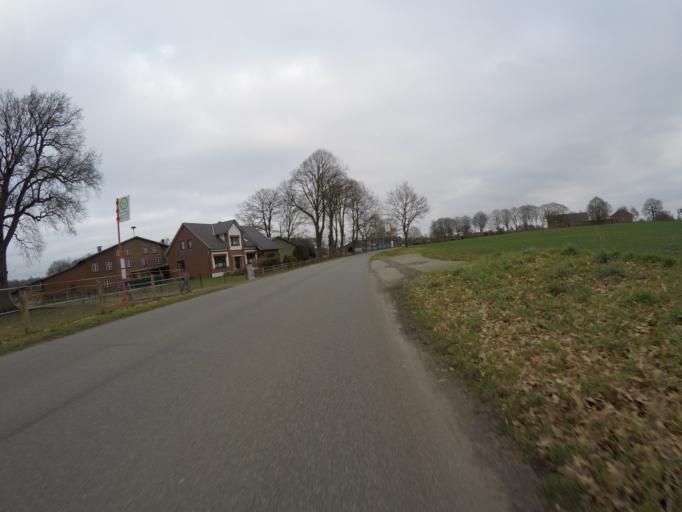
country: DE
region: Schleswig-Holstein
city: Langeln
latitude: 53.7938
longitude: 9.8464
